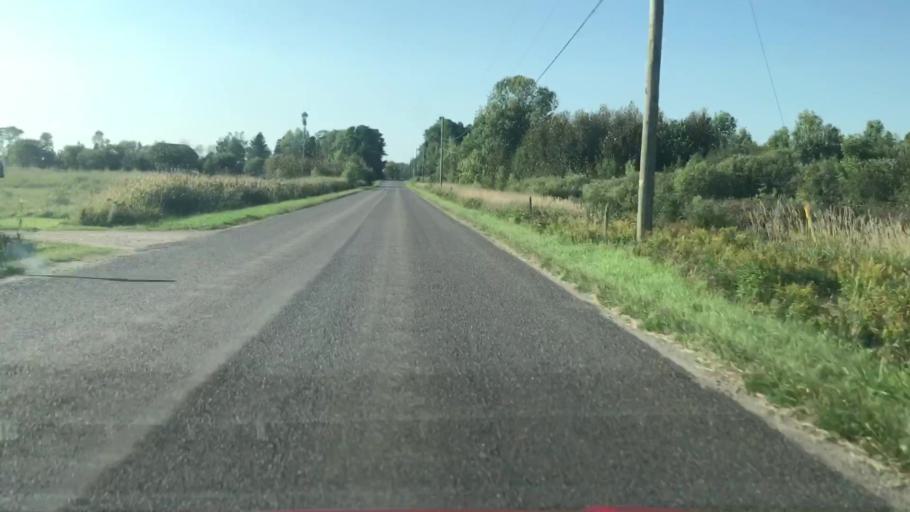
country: US
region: Michigan
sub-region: Chippewa County
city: Sault Ste. Marie
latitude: 46.2872
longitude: -84.0587
